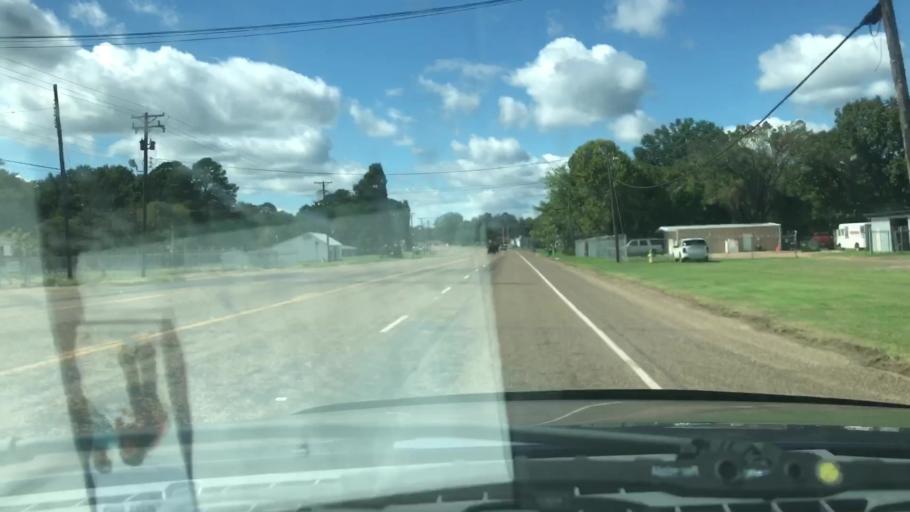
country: US
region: Texas
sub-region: Bowie County
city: Texarkana
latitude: 33.4028
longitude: -94.0703
